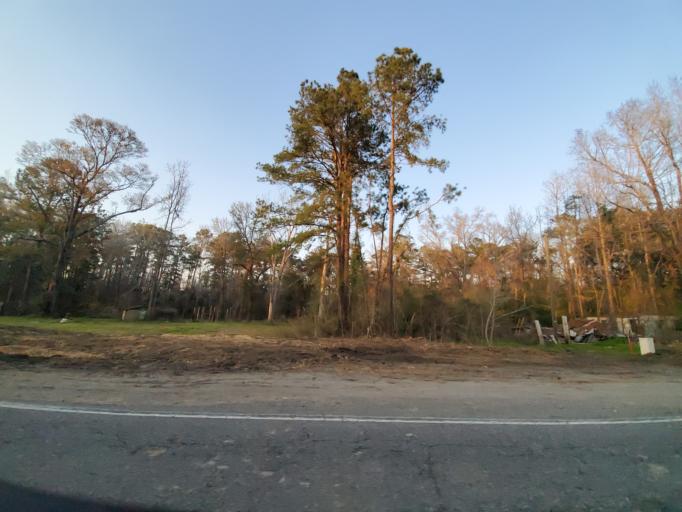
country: US
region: South Carolina
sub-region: Dorchester County
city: Ridgeville
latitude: 33.0260
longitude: -80.3879
